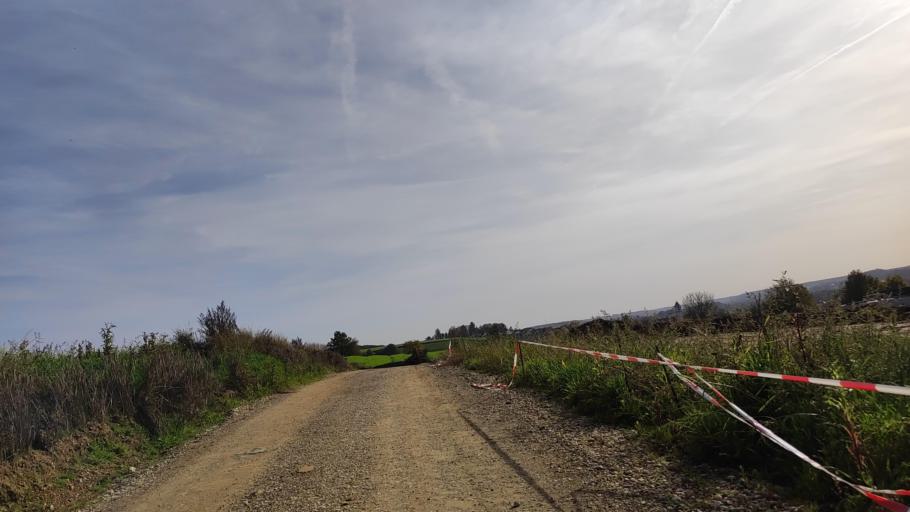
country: DE
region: Baden-Wuerttemberg
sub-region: Tuebingen Region
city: Burgrieden
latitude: 48.2316
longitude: 9.9508
